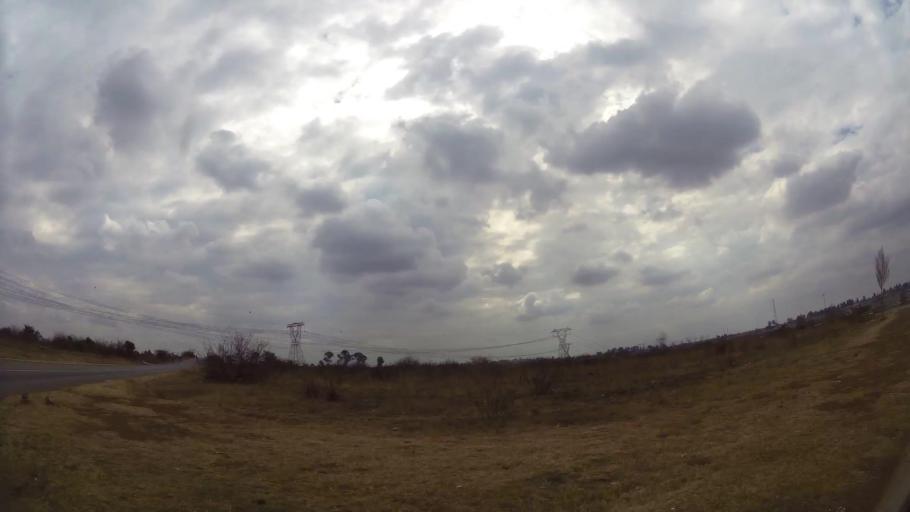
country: ZA
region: Gauteng
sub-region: Ekurhuleni Metropolitan Municipality
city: Germiston
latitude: -26.3800
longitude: 28.1115
